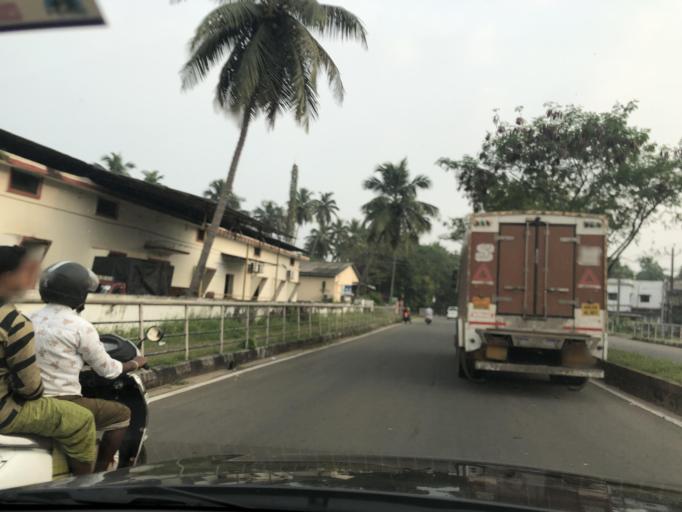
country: IN
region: Kerala
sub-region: Kozhikode
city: Kozhikode
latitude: 11.2829
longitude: 75.7613
